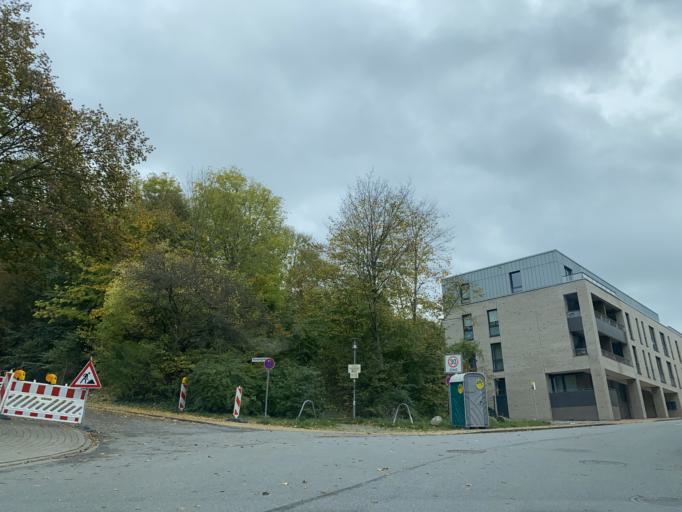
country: DE
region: Schleswig-Holstein
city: Flensburg
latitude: 54.7821
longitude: 9.4431
